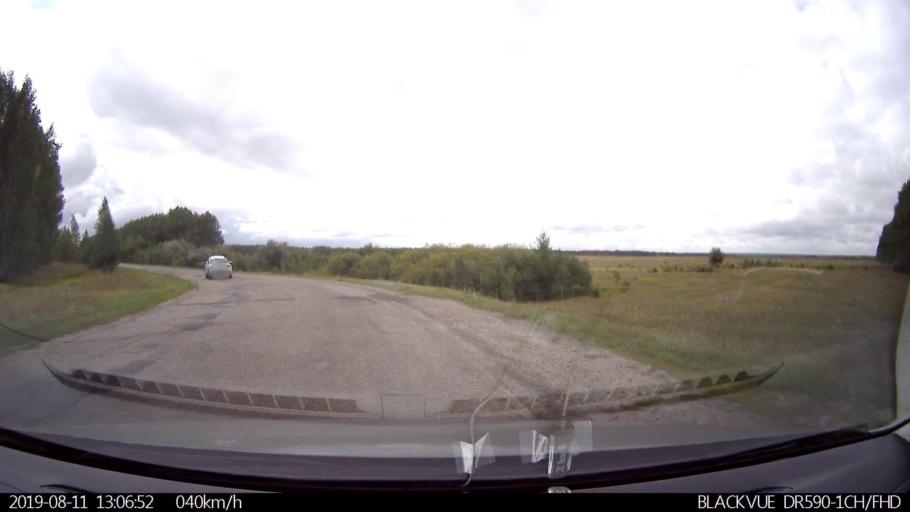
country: RU
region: Ulyanovsk
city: Ignatovka
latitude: 53.8667
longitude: 47.6396
